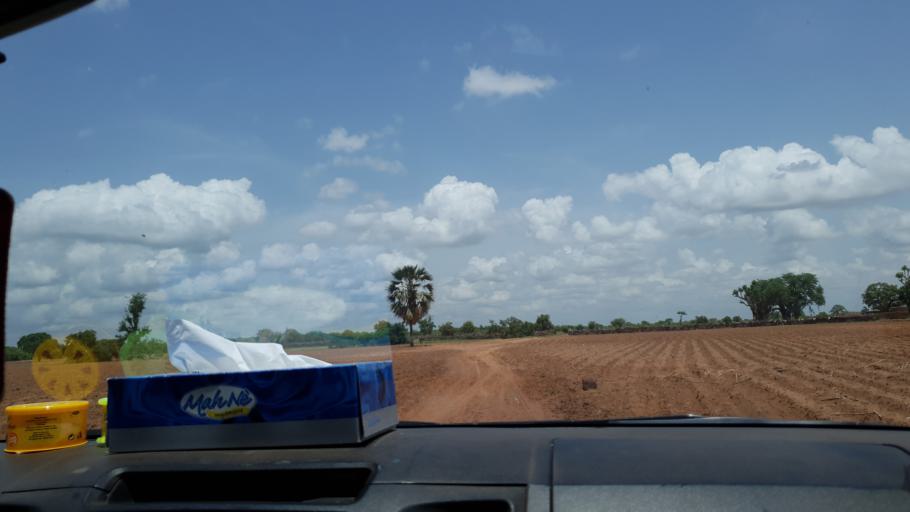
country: ML
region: Koulikoro
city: Banamba
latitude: 13.3793
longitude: -7.2028
